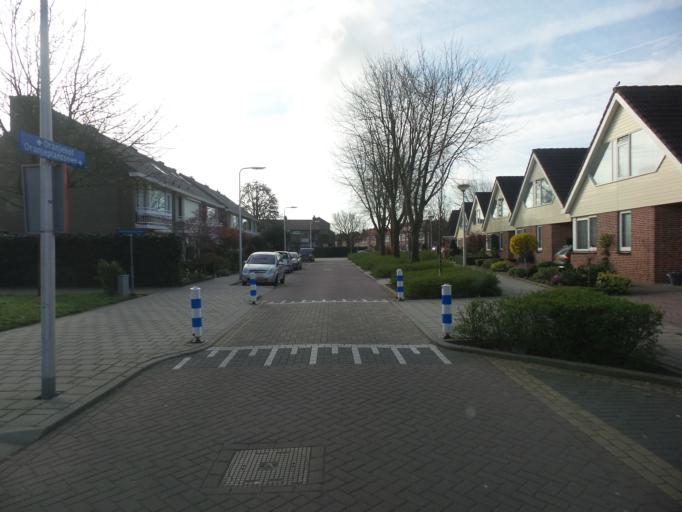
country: NL
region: South Holland
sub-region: Bodegraven-Reeuwijk
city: Bodegraven
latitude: 52.0892
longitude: 4.7437
